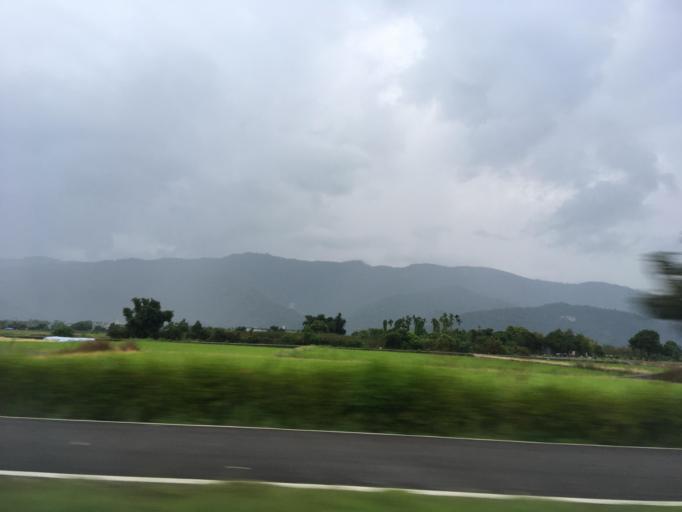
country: TW
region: Taiwan
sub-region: Yilan
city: Yilan
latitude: 24.6771
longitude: 121.6485
